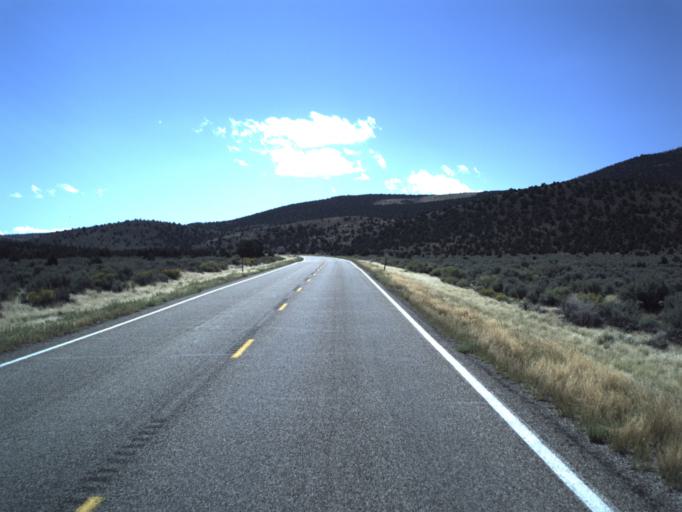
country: US
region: Utah
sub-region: Beaver County
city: Milford
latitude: 38.1377
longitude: -112.9601
